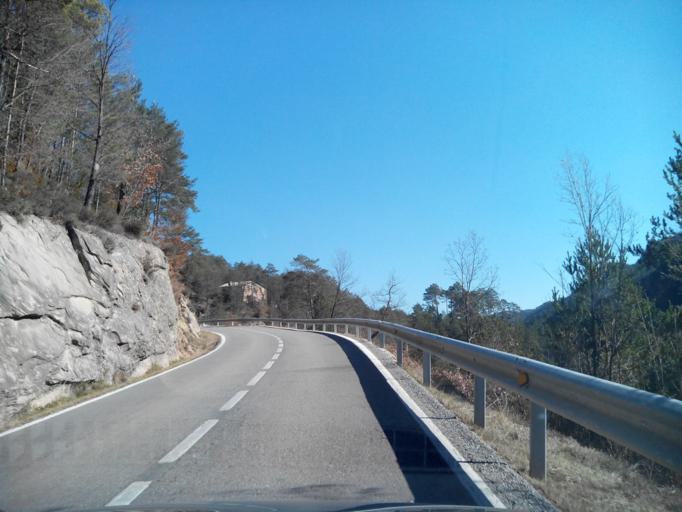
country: ES
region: Catalonia
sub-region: Provincia de Barcelona
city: Vilada
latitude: 42.1299
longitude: 1.9550
